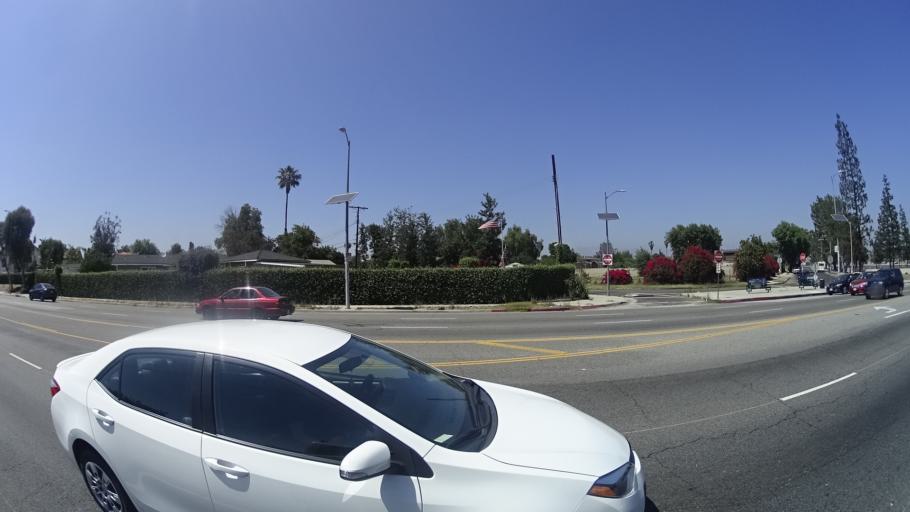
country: US
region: California
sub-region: Los Angeles County
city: Van Nuys
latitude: 34.2216
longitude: -118.4254
